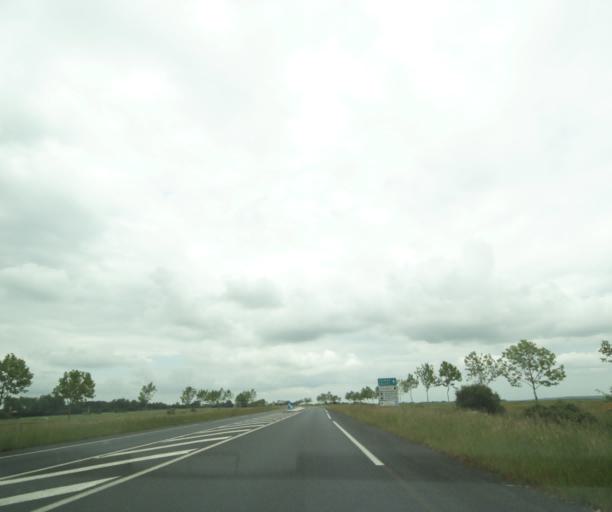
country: FR
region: Poitou-Charentes
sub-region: Departement des Deux-Sevres
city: Saint-Varent
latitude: 46.8998
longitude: -0.1915
